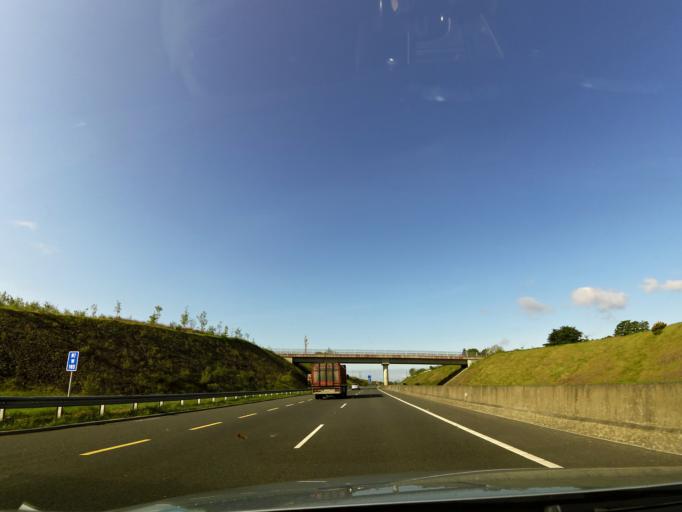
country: IE
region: Munster
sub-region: North Tipperary
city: Newport
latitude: 52.7660
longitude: -8.3910
